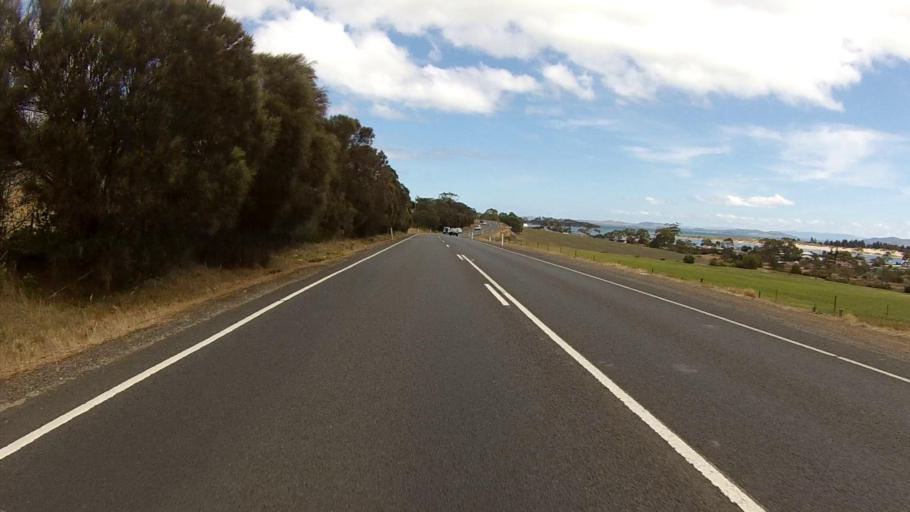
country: AU
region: Tasmania
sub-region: Sorell
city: Sorell
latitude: -42.8354
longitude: 147.6241
